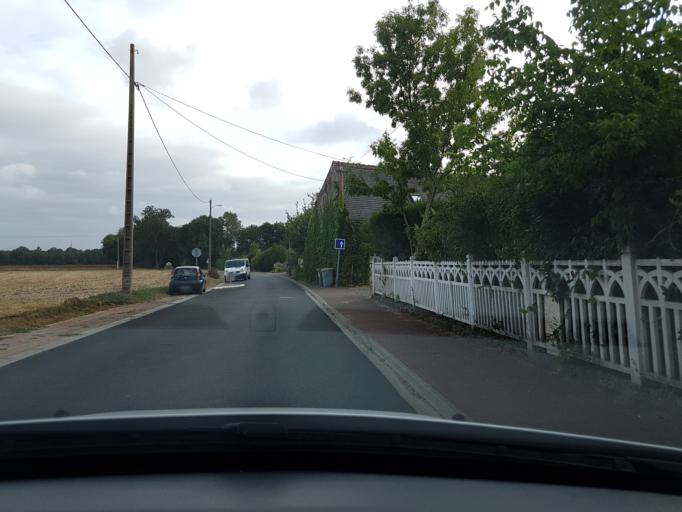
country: FR
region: Centre
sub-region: Departement d'Indre-et-Loire
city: Azay-sur-Cher
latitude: 47.3535
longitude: 0.8519
